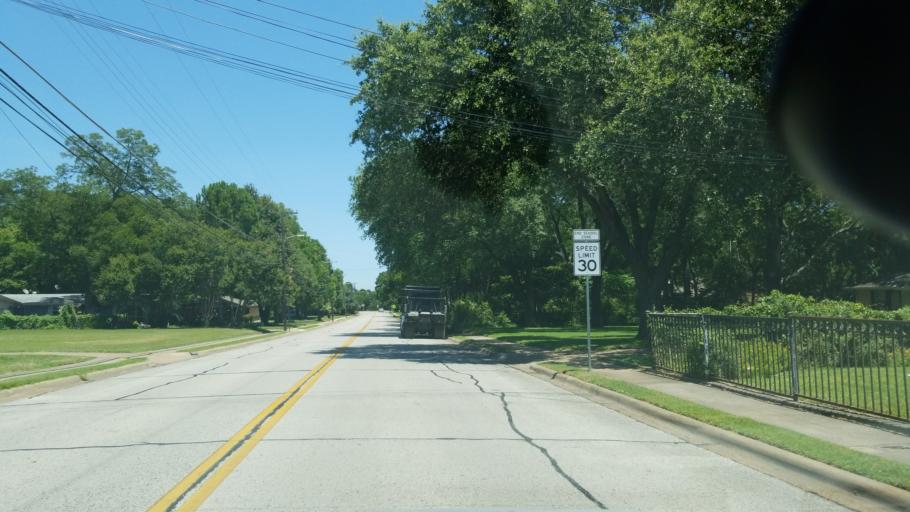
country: US
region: Texas
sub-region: Dallas County
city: Irving
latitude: 32.8230
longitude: -96.9292
